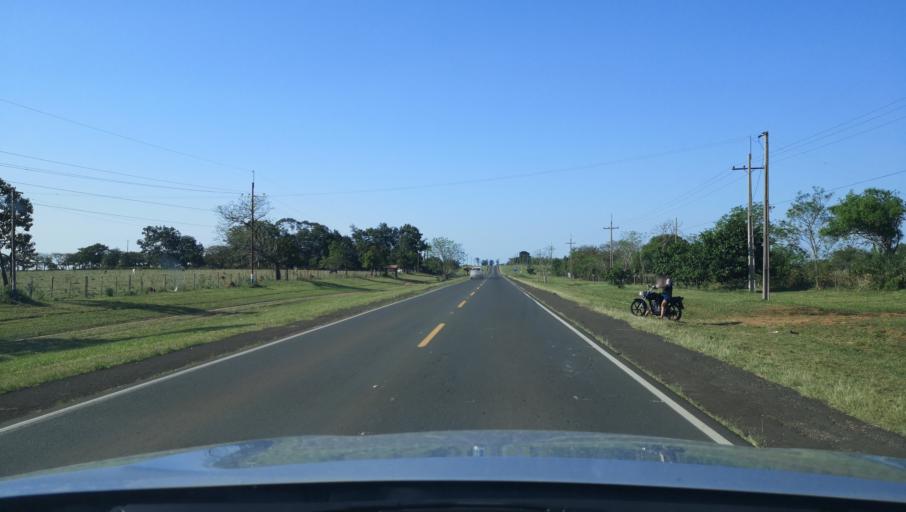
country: PY
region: Misiones
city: Santa Maria
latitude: -26.8177
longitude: -57.0249
